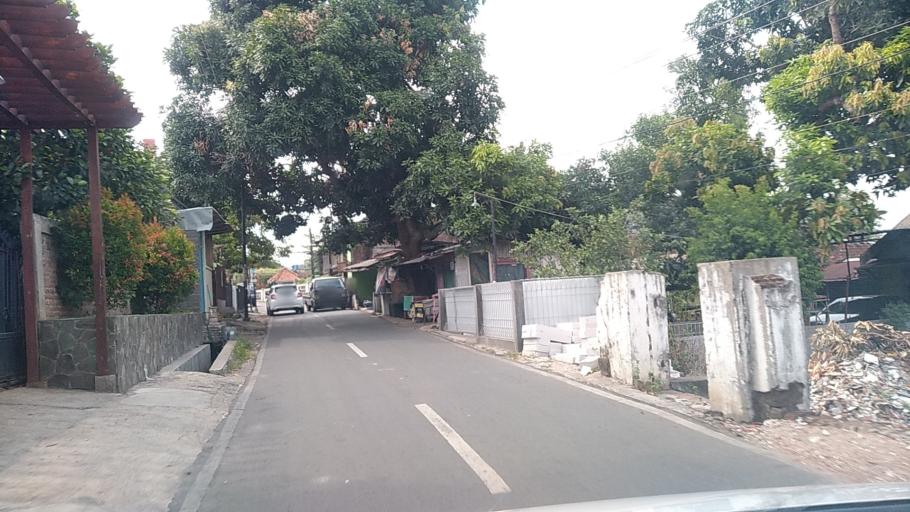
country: ID
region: Central Java
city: Semarang
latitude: -7.0340
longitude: 110.4199
